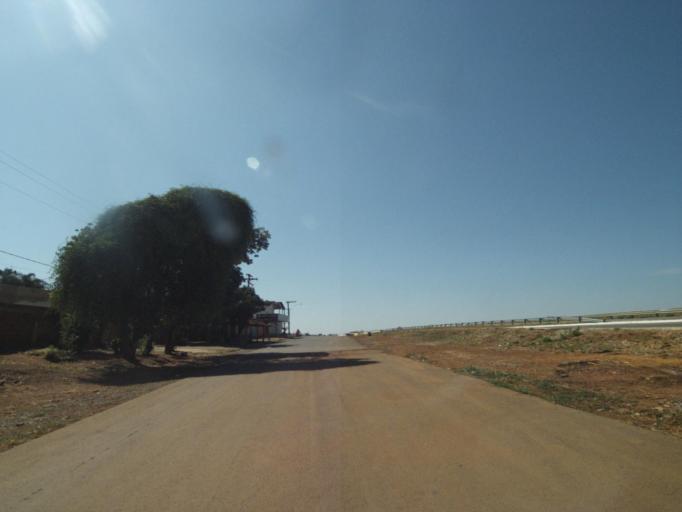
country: BR
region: Goias
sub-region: Anapolis
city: Anapolis
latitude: -16.1887
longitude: -49.0366
